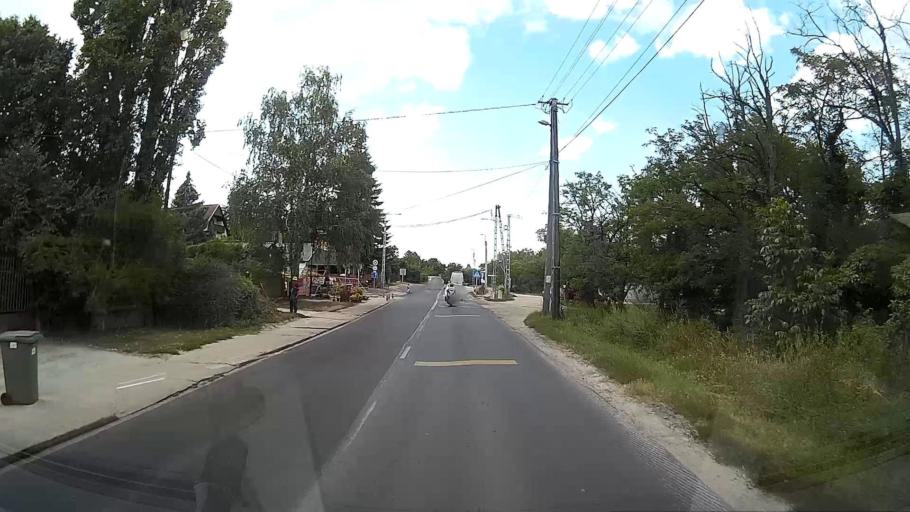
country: HU
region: Pest
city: Tahitotfalu
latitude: 47.7423
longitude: 19.0850
